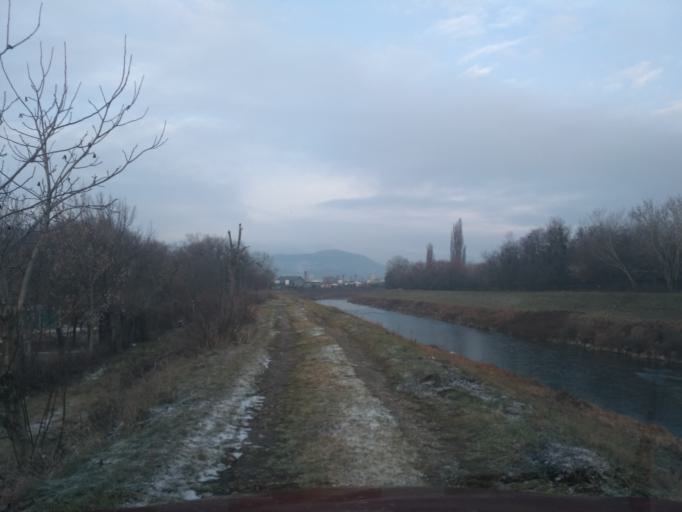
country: SK
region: Kosicky
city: Kosice
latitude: 48.7305
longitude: 21.2704
